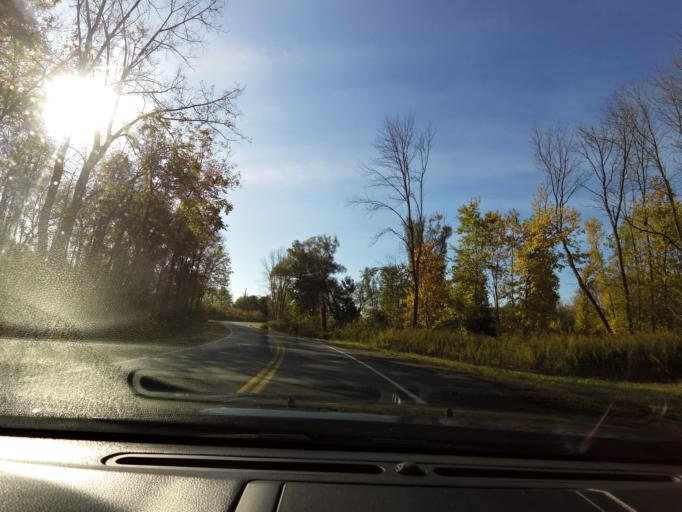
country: US
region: New York
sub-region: Livingston County
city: Mount Morris
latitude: 42.7656
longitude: -77.8746
